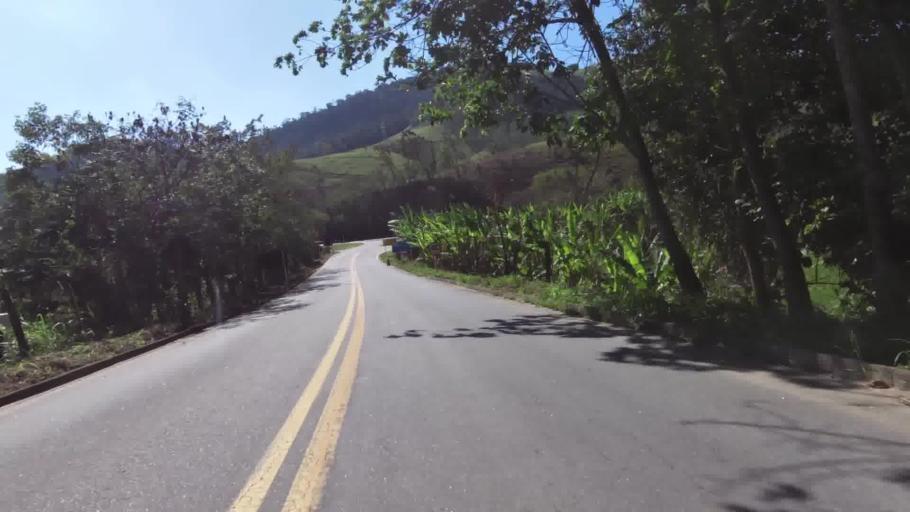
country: BR
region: Espirito Santo
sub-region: Rio Novo Do Sul
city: Rio Novo do Sul
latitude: -20.8677
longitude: -40.9074
